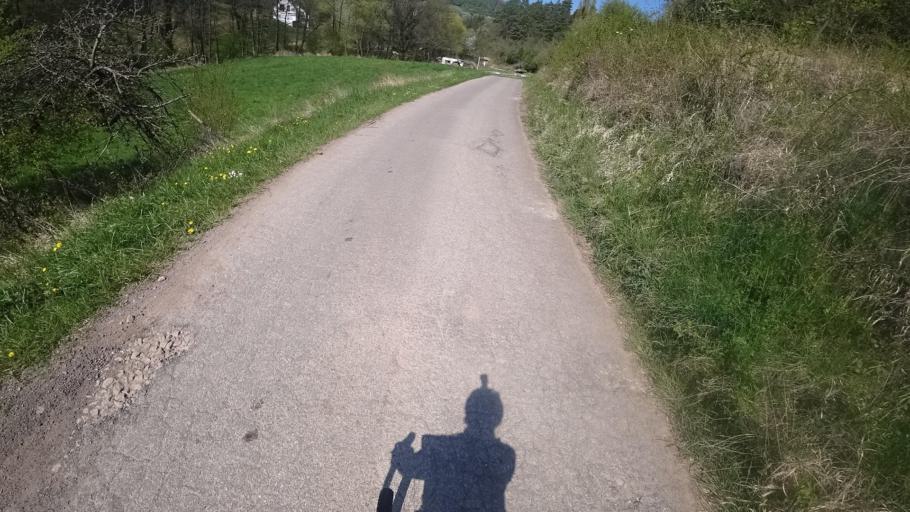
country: DE
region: Rheinland-Pfalz
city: Tawern
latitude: 49.6775
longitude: 6.5095
